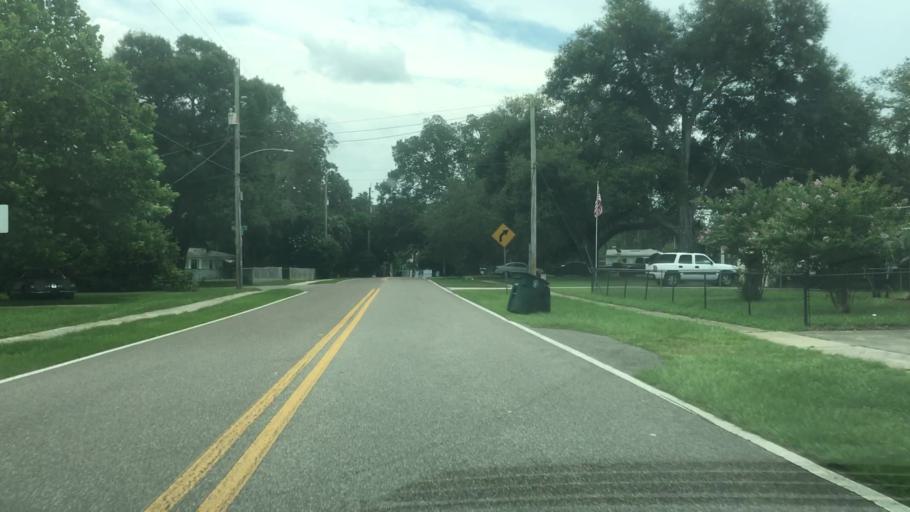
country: US
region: Florida
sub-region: Duval County
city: Jacksonville
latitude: 30.2942
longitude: -81.5496
